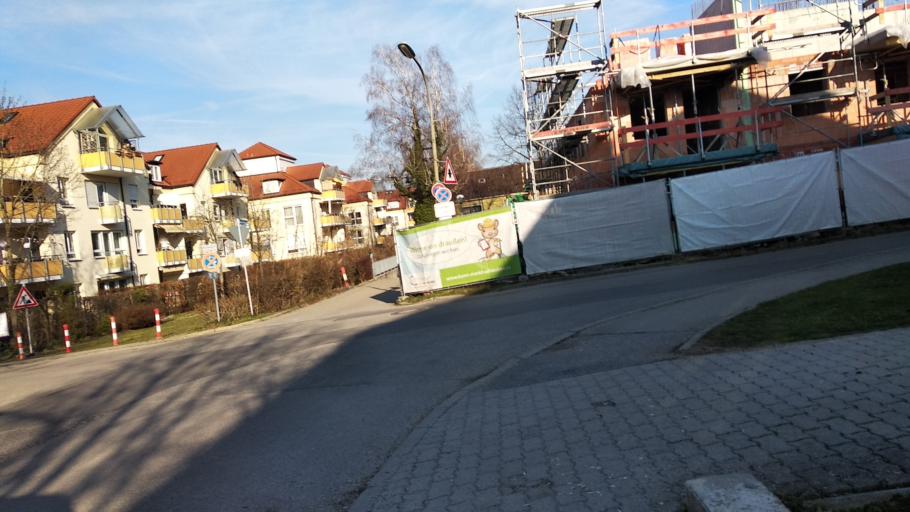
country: DE
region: Bavaria
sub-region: Upper Bavaria
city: Markt Schwaben
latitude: 48.1878
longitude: 11.8655
